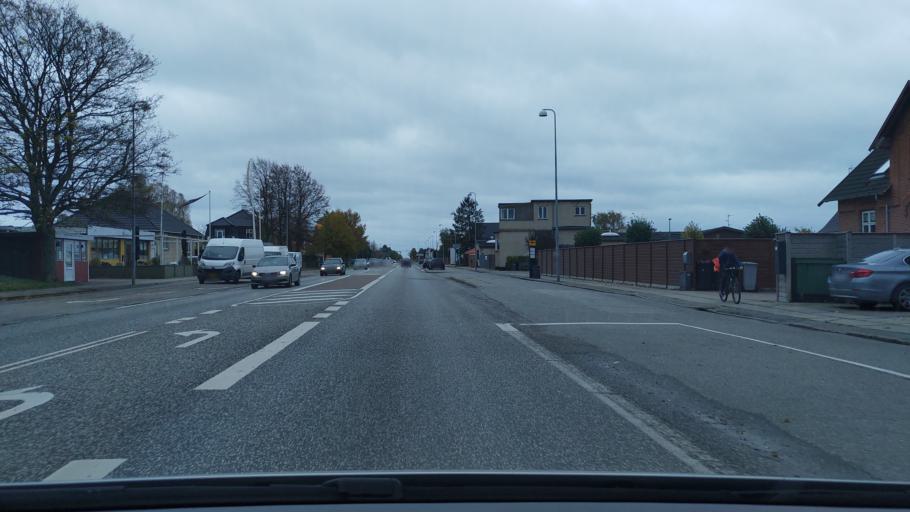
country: DK
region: Capital Region
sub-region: Tarnby Kommune
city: Tarnby
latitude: 55.6263
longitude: 12.6242
